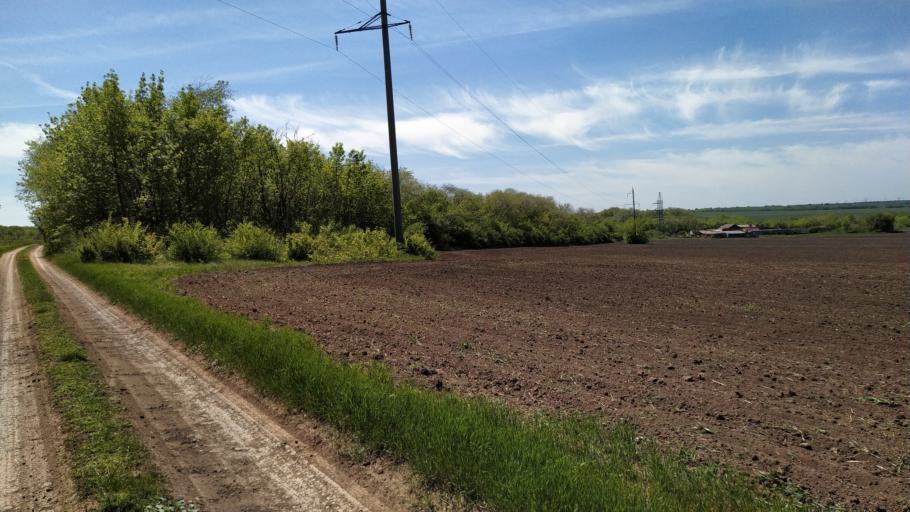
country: RU
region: Rostov
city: Kuleshovka
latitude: 47.0297
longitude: 39.6319
